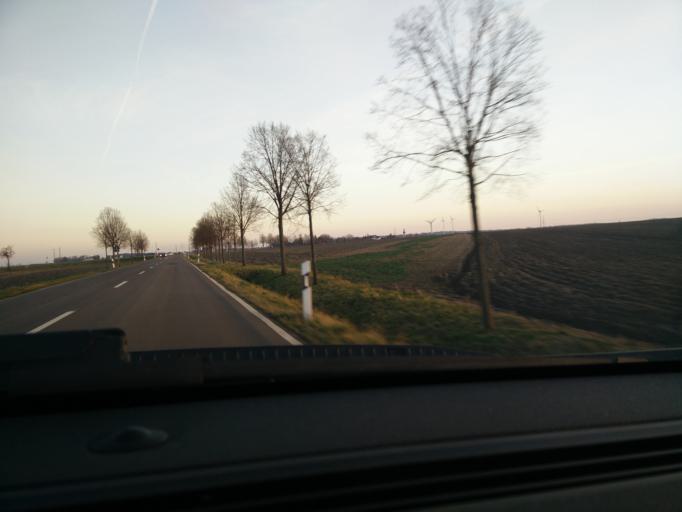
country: DE
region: Saxony
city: Bad Lausick
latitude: 51.1101
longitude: 12.6872
